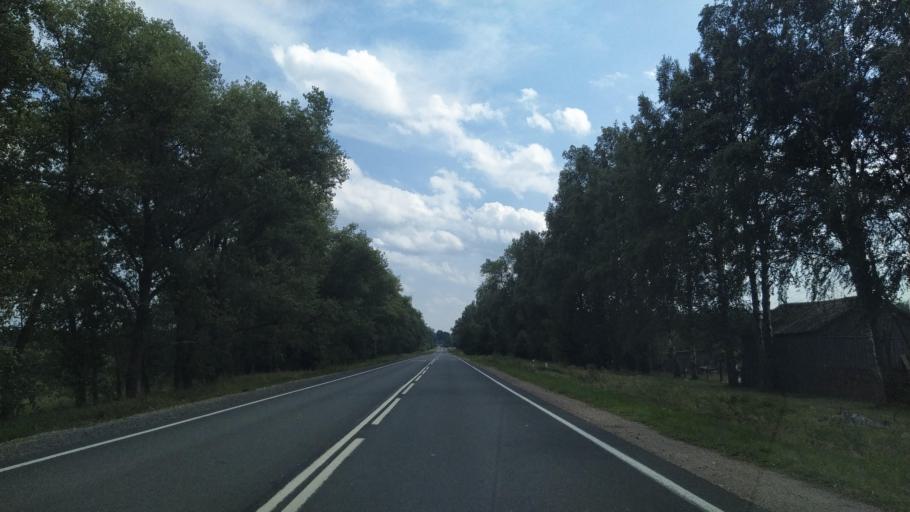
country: RU
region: Pskov
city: Pskov
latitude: 57.7536
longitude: 28.7774
